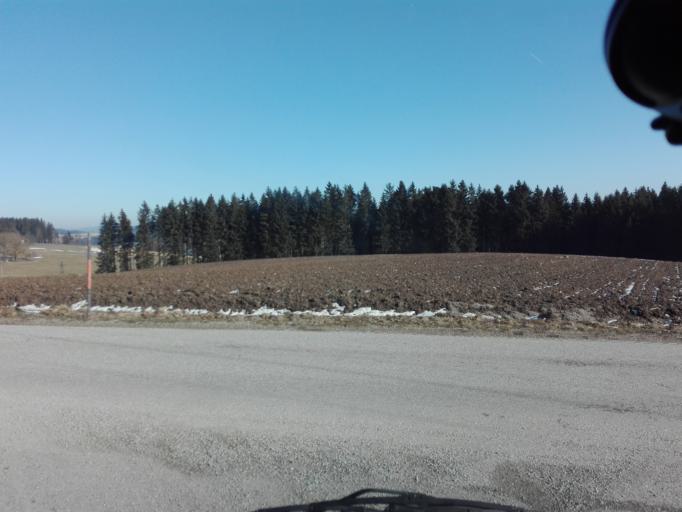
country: AT
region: Upper Austria
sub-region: Politischer Bezirk Urfahr-Umgebung
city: Sonnberg im Muehlkreis
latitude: 48.4618
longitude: 14.3279
